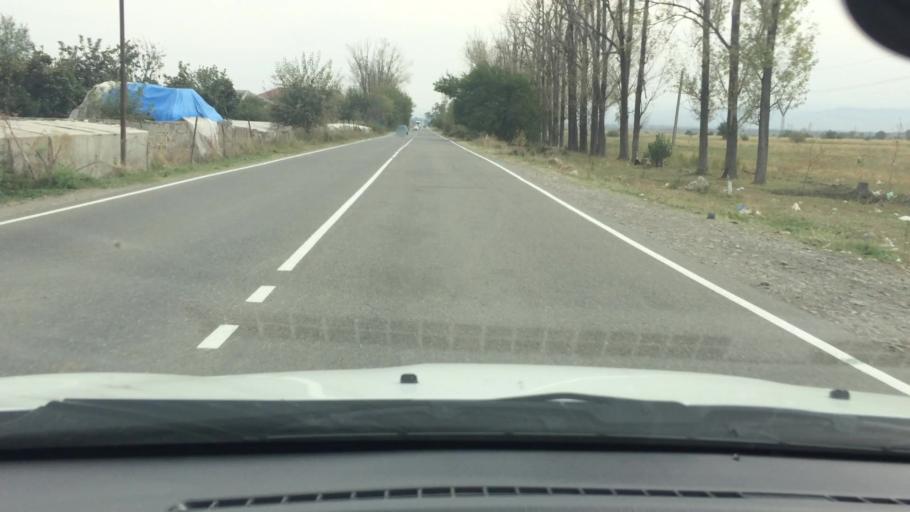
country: GE
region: Kvemo Kartli
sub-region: Gardabani
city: Gardabani
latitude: 41.4472
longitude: 44.9960
